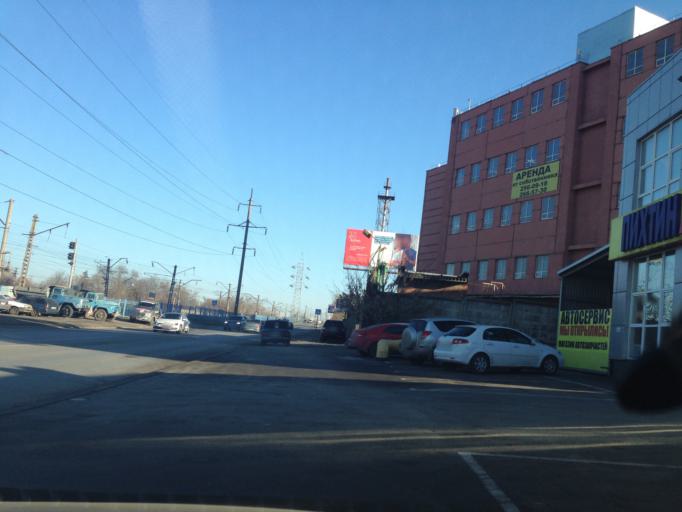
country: RU
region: Rostov
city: Rostov-na-Donu
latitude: 47.2437
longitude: 39.7286
